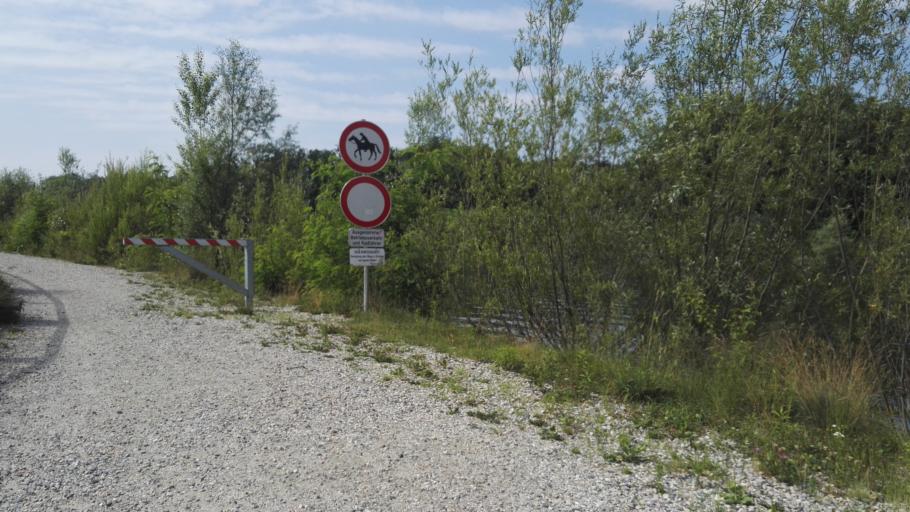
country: AT
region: Styria
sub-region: Politischer Bezirk Graz-Umgebung
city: Feldkirchen bei Graz
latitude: 47.0111
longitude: 15.4618
